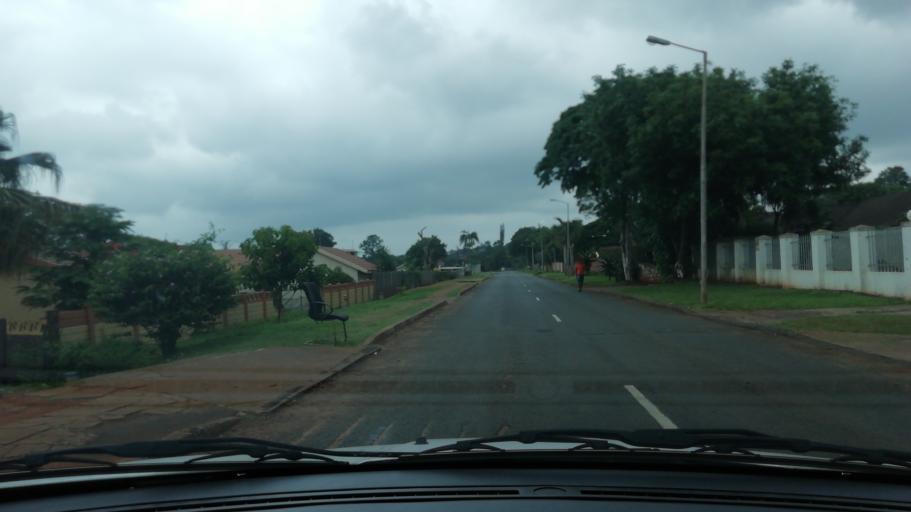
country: ZA
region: KwaZulu-Natal
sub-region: uThungulu District Municipality
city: Empangeni
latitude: -28.7593
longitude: 31.8985
